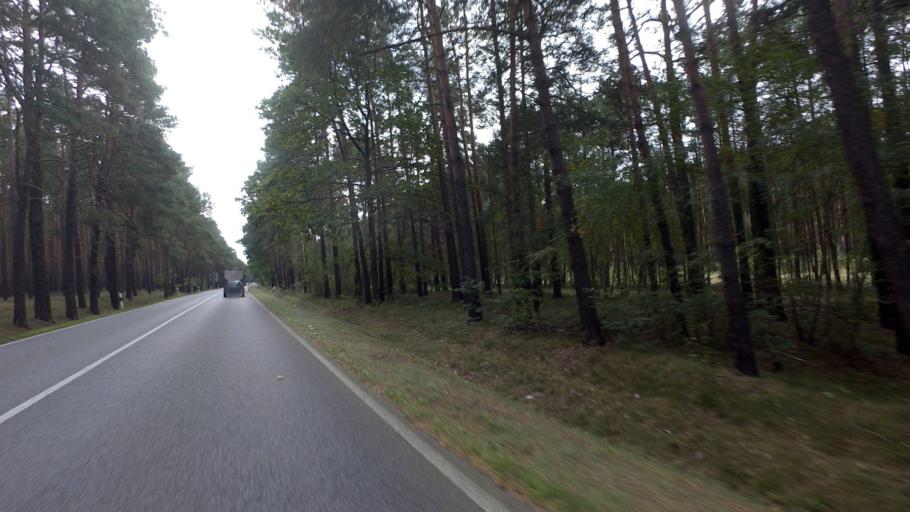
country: DE
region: Brandenburg
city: Kasel-Golzig
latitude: 51.9265
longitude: 13.6659
